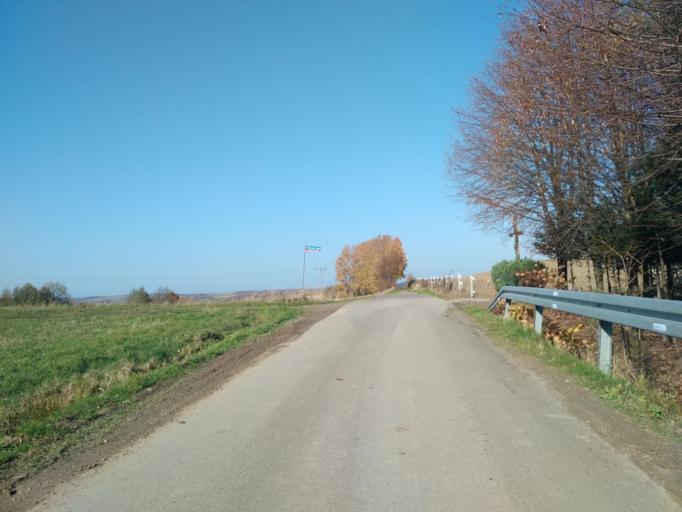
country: PL
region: Subcarpathian Voivodeship
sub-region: Powiat rzeszowski
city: Blazowa
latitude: 49.8561
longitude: 22.0801
